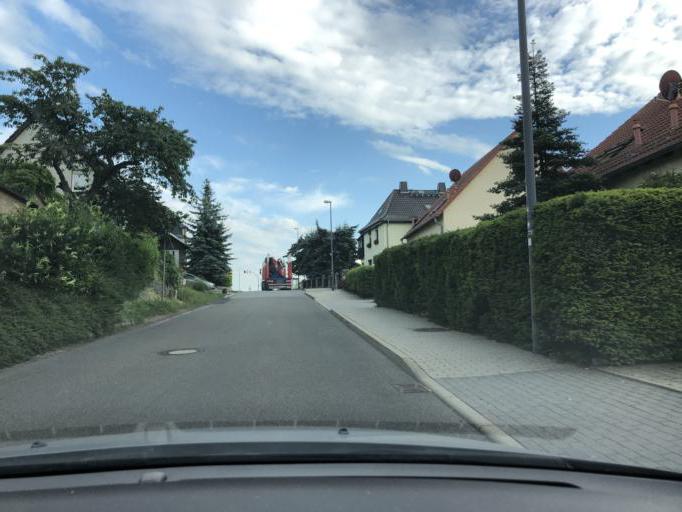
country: DE
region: Saxony
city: Freital
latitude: 51.0420
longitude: 13.6253
